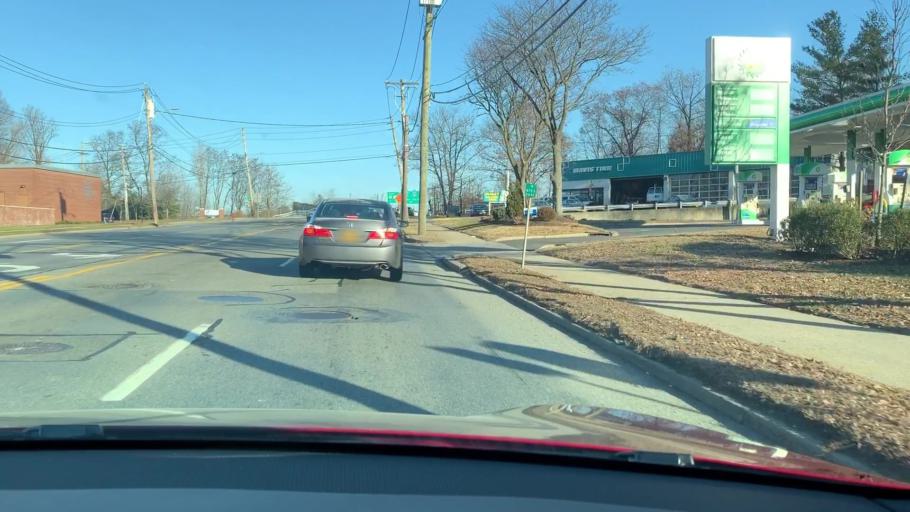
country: US
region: New York
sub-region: Westchester County
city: Tarrytown
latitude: 41.0613
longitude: -73.8621
